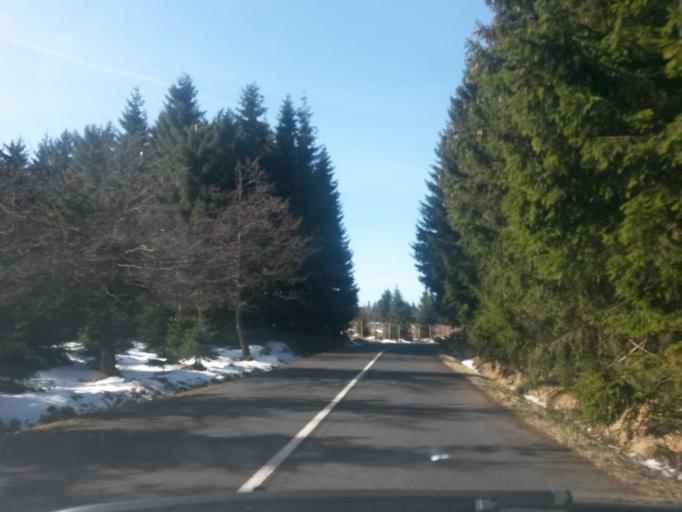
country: DE
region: Saxony
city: Kurort Oberwiesenthal
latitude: 50.3981
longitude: 13.0123
